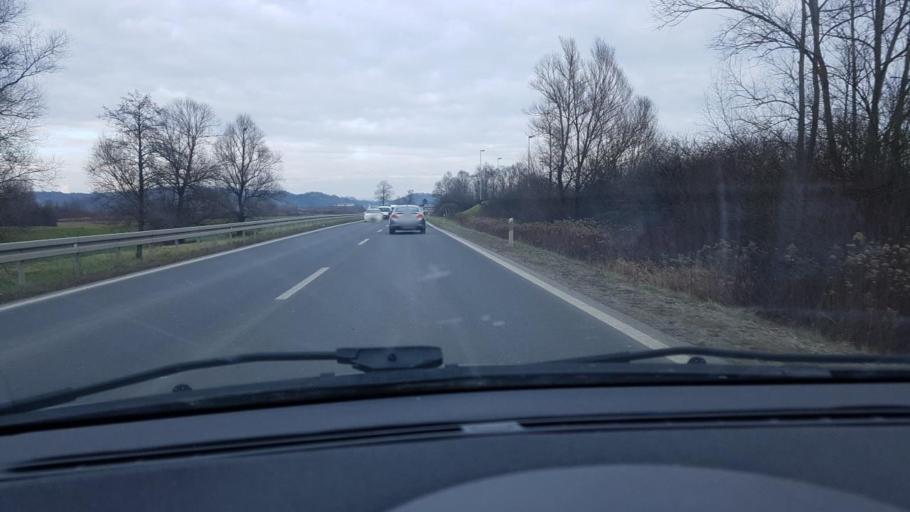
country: HR
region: Zagrebacka
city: Jakovlje
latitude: 45.9981
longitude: 15.8601
